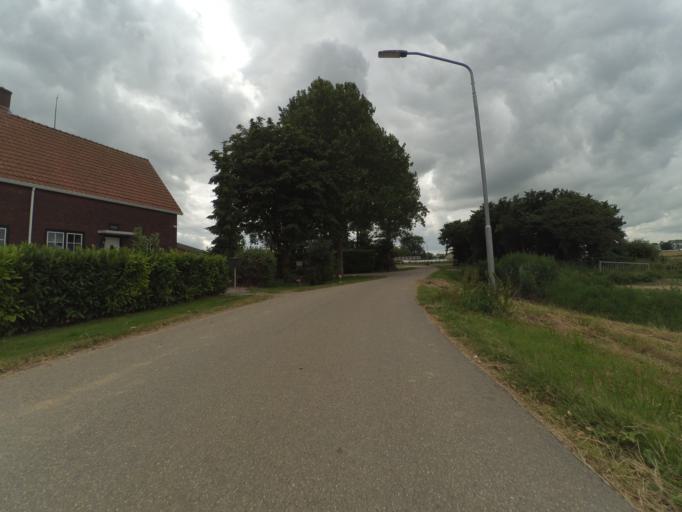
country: NL
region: South Holland
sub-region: Gemeente Dordrecht
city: Dordrecht
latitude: 51.7437
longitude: 4.6427
